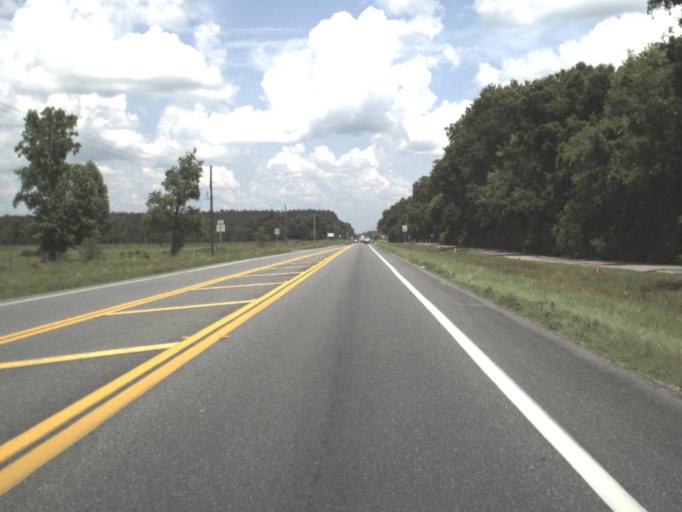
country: US
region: Florida
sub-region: Suwannee County
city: Wellborn
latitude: 29.9524
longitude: -82.8587
